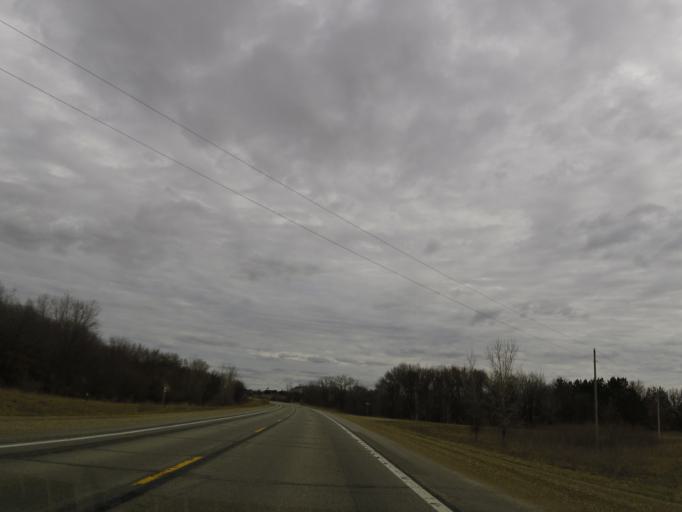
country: US
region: Iowa
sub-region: Howard County
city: Cresco
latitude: 43.4615
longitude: -92.3086
